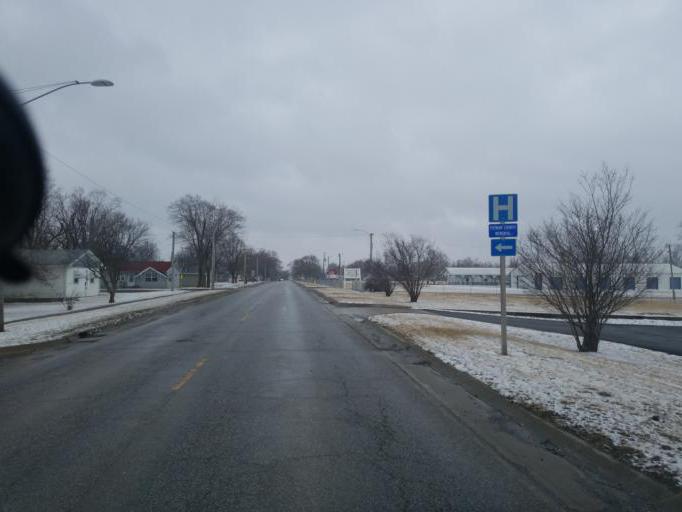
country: US
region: Missouri
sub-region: Putnam County
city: Unionville
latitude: 40.4827
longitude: -93.0092
